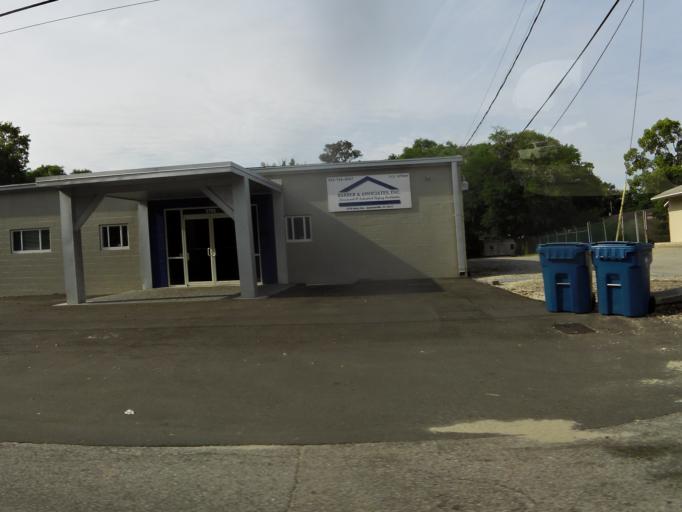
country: US
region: Florida
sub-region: Duval County
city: Jacksonville
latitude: 30.3359
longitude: -81.6004
